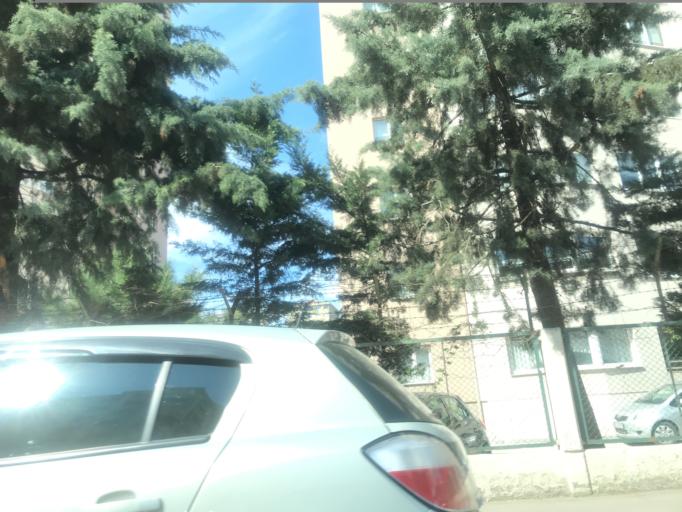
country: TR
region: Istanbul
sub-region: Atasehir
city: Atasehir
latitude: 40.9751
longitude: 29.1119
